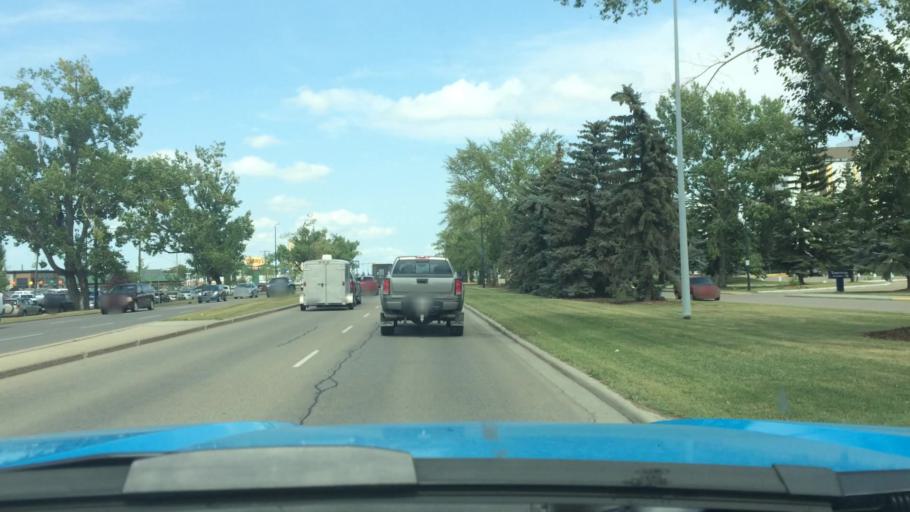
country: CA
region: Alberta
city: Red Deer
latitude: 52.2456
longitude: -113.8139
